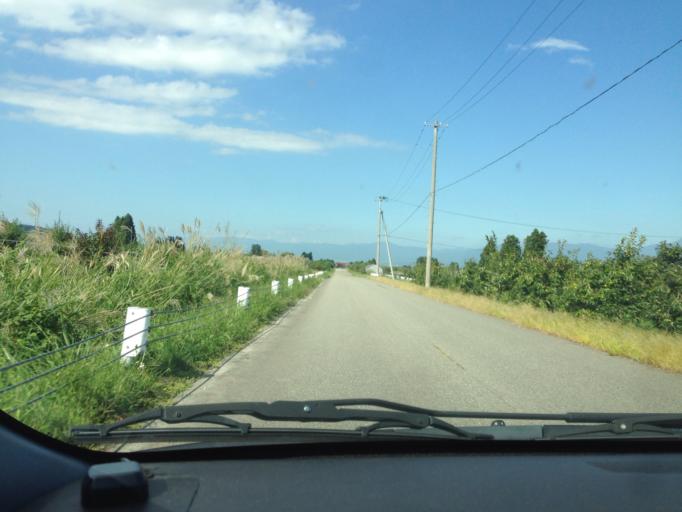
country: JP
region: Fukushima
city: Kitakata
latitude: 37.4365
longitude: 139.8089
